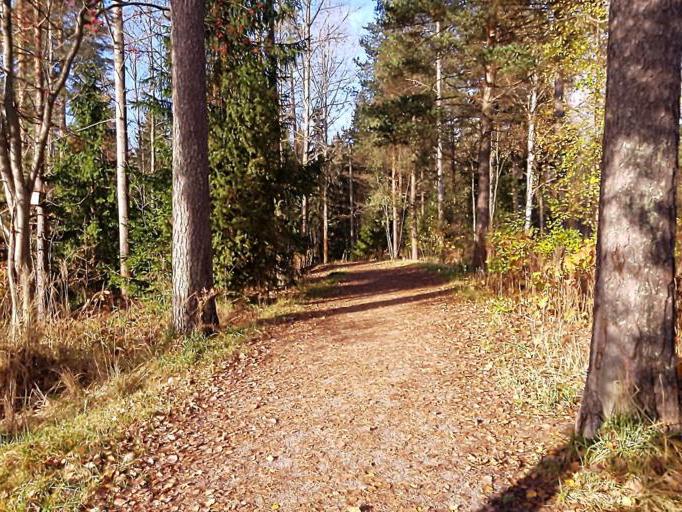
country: FI
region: Uusimaa
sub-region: Helsinki
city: Teekkarikylae
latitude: 60.2536
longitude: 24.8938
